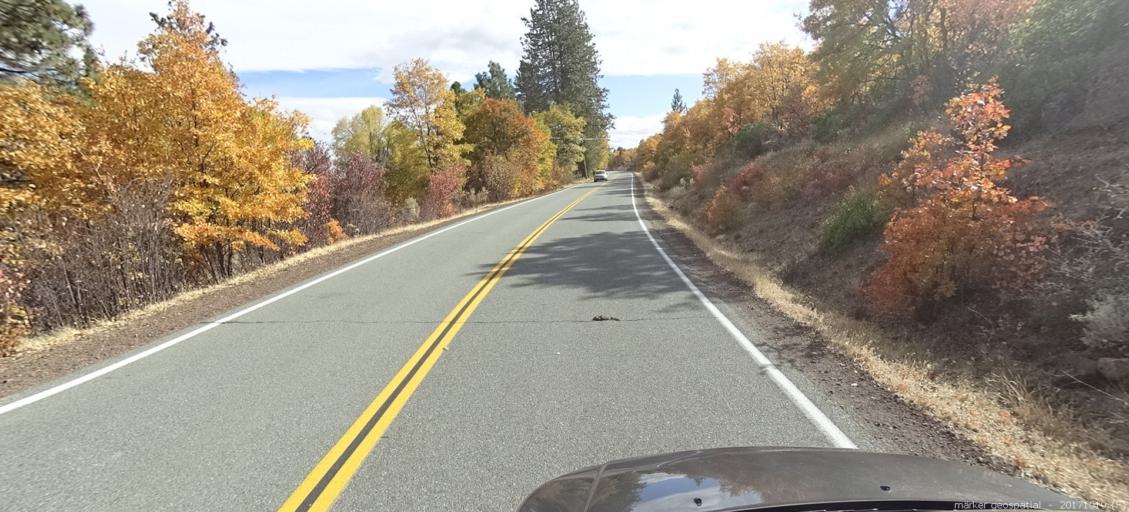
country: US
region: California
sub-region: Shasta County
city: Burney
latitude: 41.0241
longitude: -121.4747
